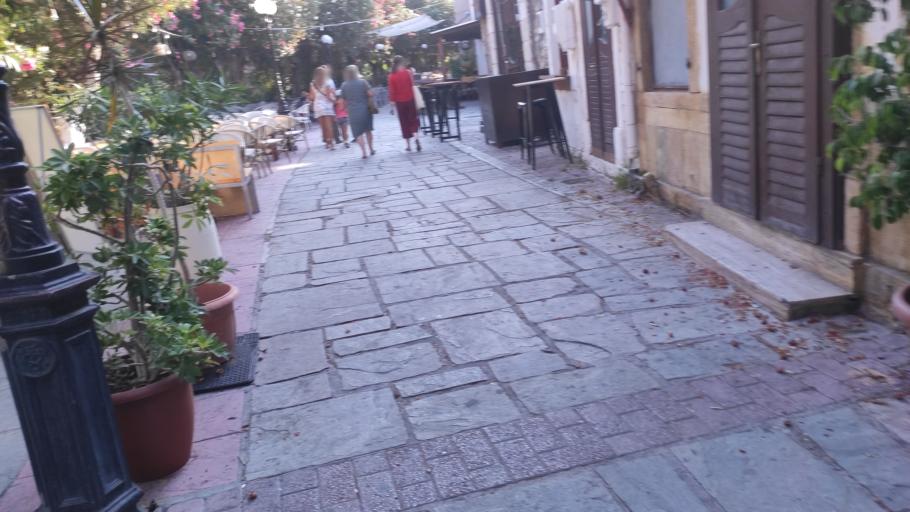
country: GR
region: South Aegean
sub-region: Nomos Dodekanisou
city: Kos
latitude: 36.8939
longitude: 27.2900
